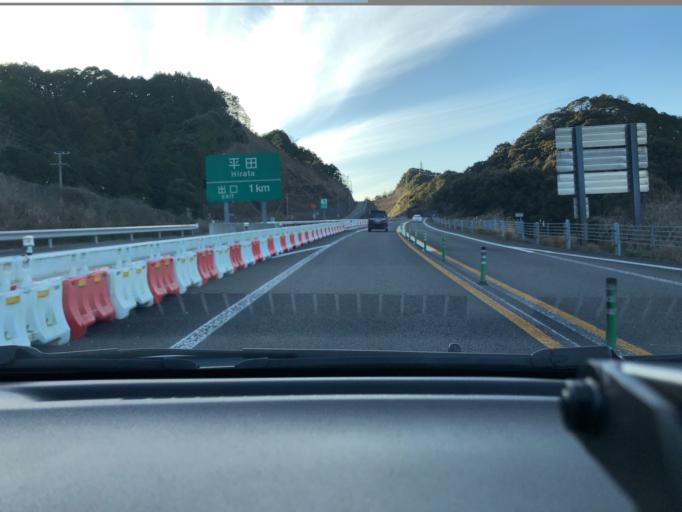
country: JP
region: Kochi
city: Sukumo
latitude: 32.9573
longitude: 132.8274
